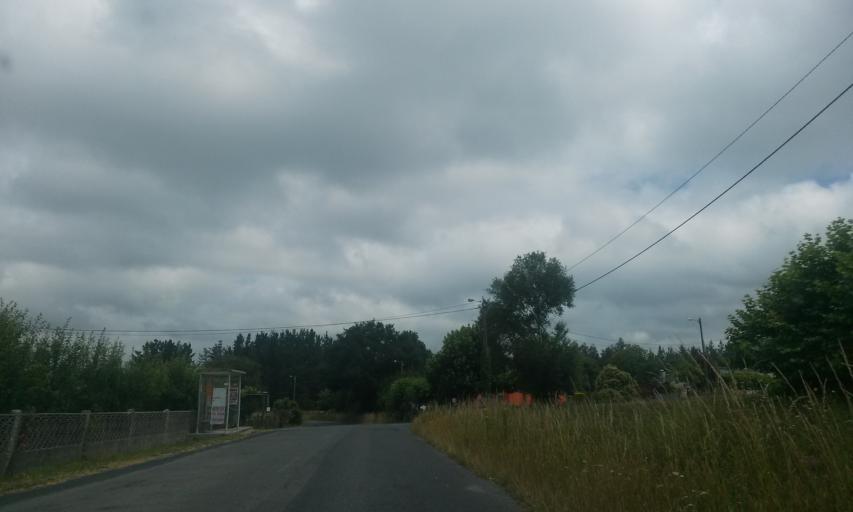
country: ES
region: Galicia
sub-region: Provincia de Lugo
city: Friol
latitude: 43.0865
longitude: -7.8106
